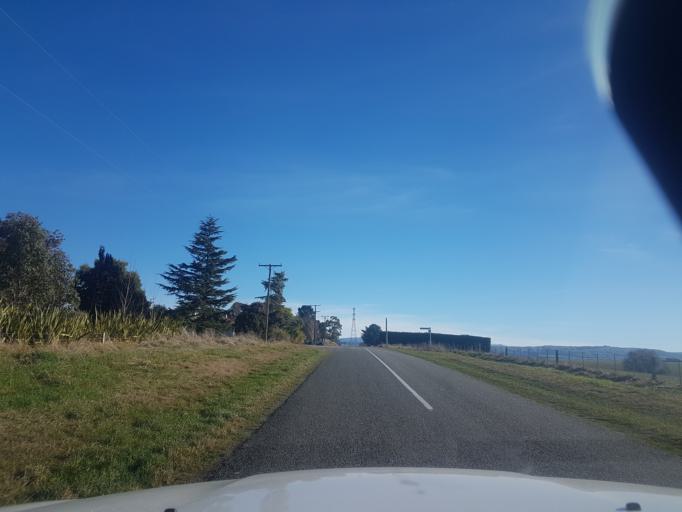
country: NZ
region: Canterbury
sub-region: Timaru District
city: Pleasant Point
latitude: -44.2533
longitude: 171.0441
